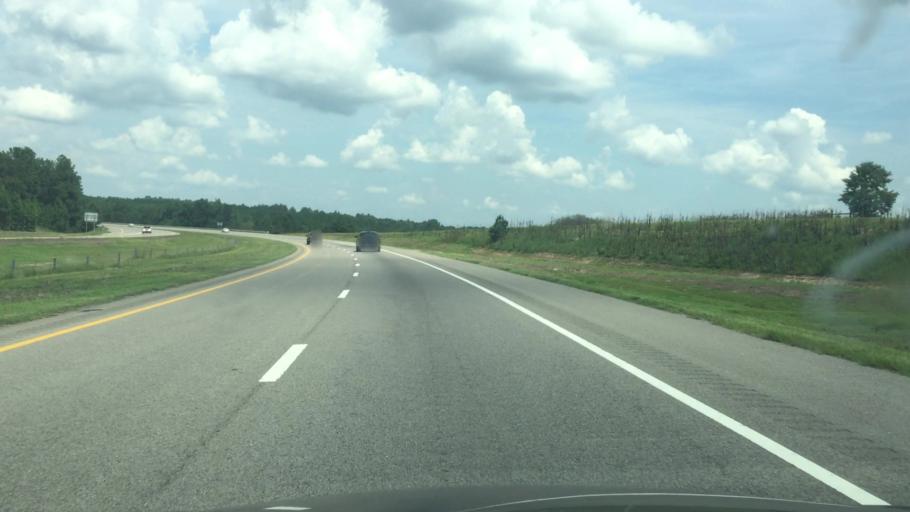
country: US
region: North Carolina
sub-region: Richmond County
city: Ellerbe
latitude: 35.1755
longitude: -79.7129
